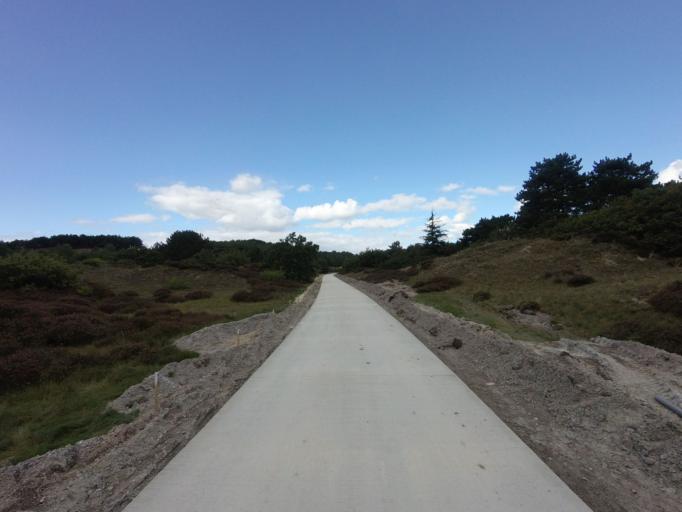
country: NL
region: North Holland
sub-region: Gemeente Bergen
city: Egmond aan Zee
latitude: 52.7123
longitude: 4.6642
